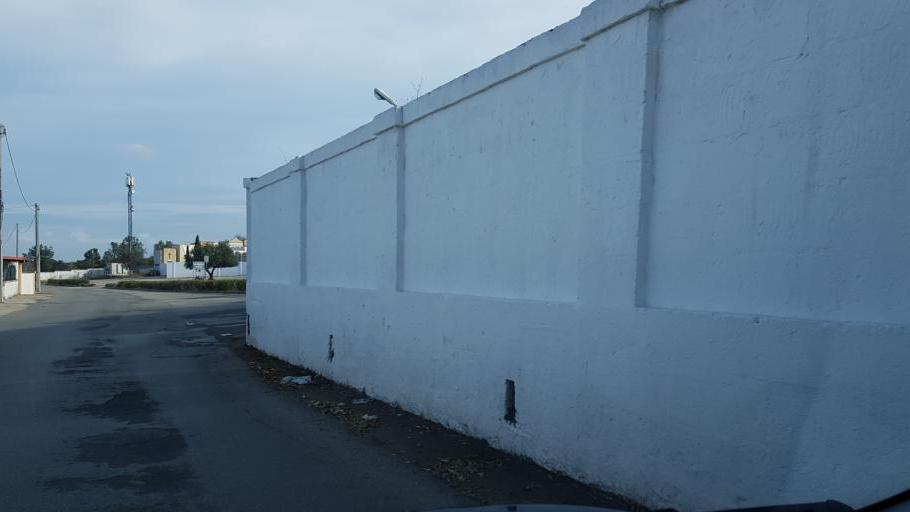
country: IT
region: Apulia
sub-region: Provincia di Brindisi
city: Oria
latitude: 40.5003
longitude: 17.6511
